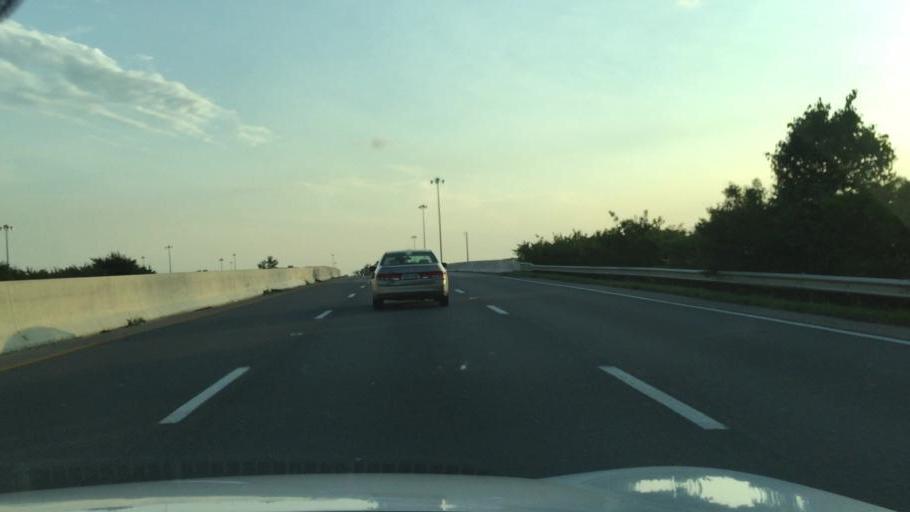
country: US
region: Ohio
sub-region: Franklin County
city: Grandview Heights
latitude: 39.9724
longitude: -83.0189
